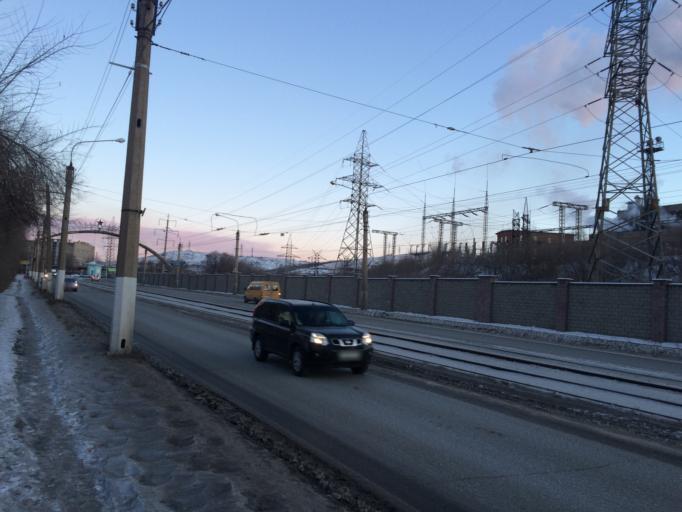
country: RU
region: Chelyabinsk
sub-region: Gorod Magnitogorsk
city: Magnitogorsk
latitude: 53.3982
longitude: 59.0190
